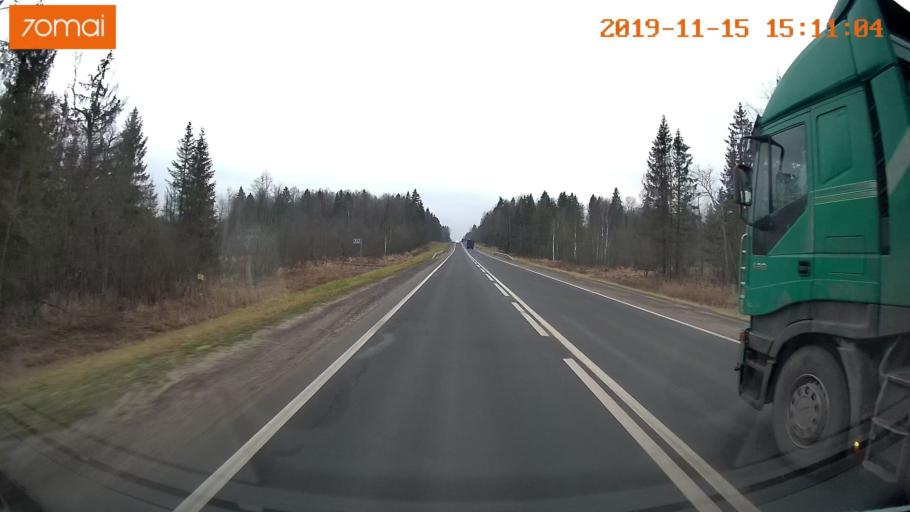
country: RU
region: Jaroslavl
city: Prechistoye
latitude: 58.3413
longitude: 40.2473
